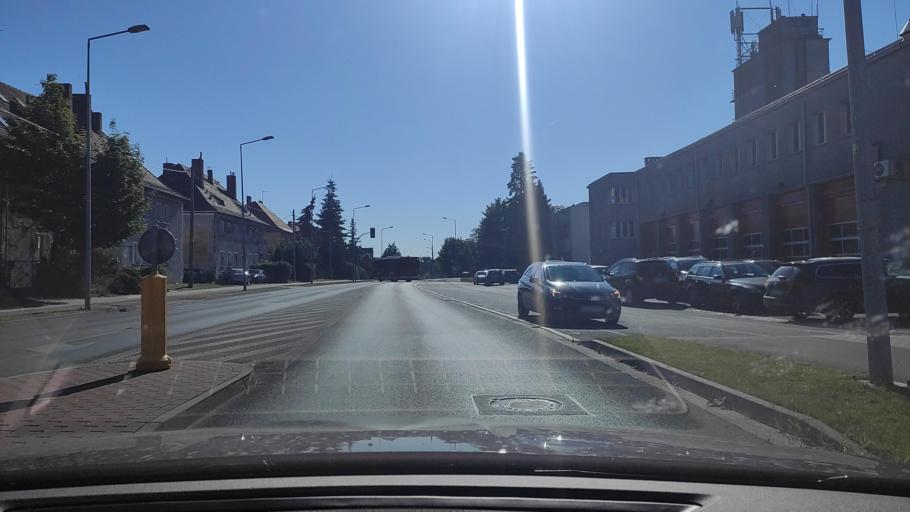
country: PL
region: Greater Poland Voivodeship
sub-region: Powiat poznanski
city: Lubon
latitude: 52.3694
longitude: 16.9079
